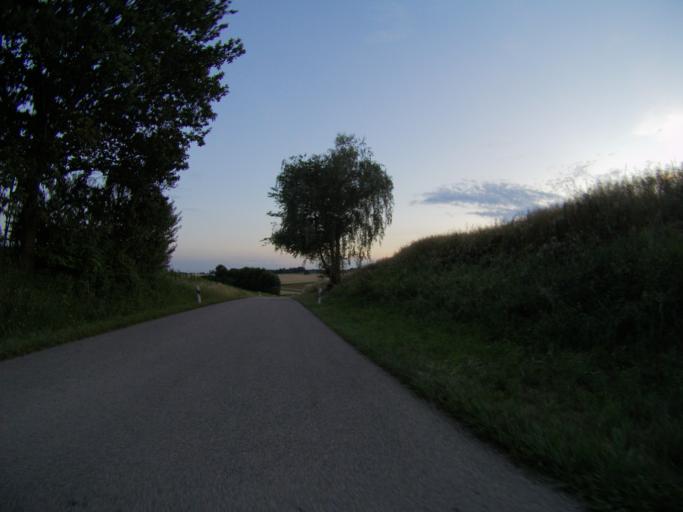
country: DE
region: Bavaria
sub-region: Upper Bavaria
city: Marzling
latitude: 48.4334
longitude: 11.7861
